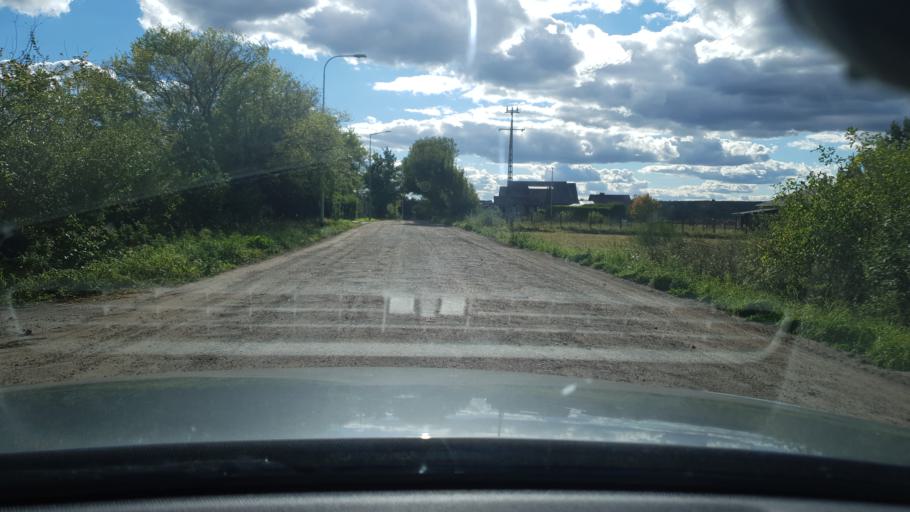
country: PL
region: Pomeranian Voivodeship
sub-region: Powiat wejherowski
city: Reda
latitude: 54.5781
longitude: 18.3113
